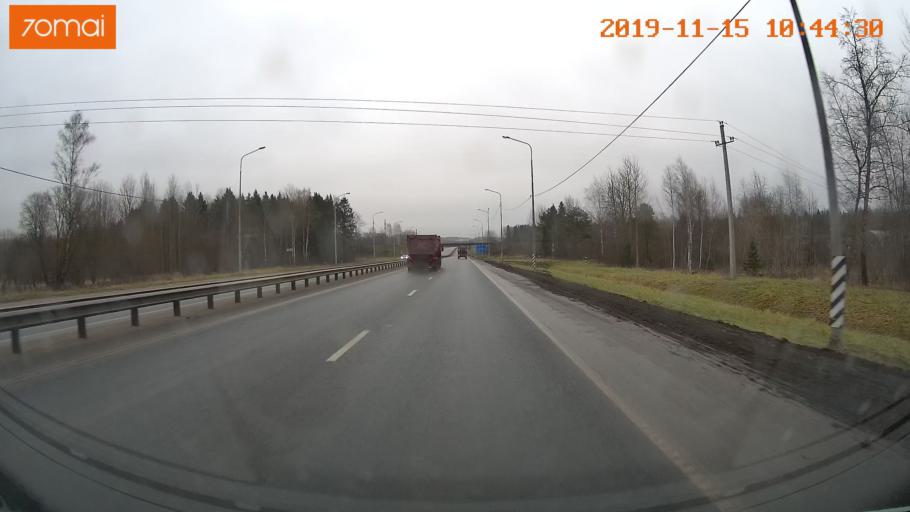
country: RU
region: Vologda
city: Sheksna
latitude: 59.2114
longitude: 38.5594
